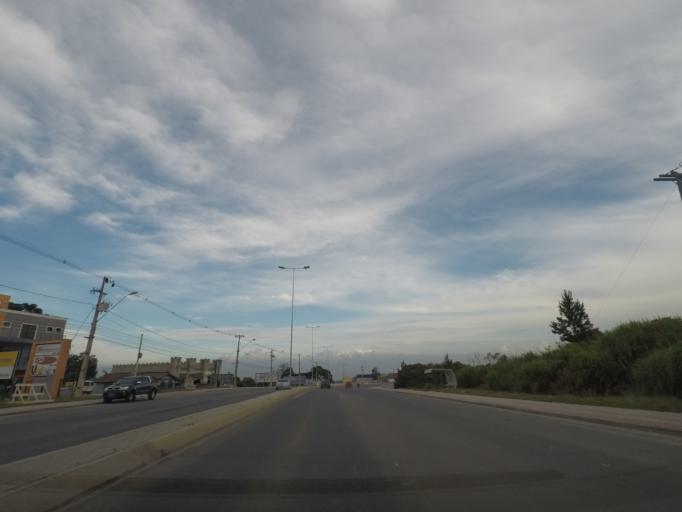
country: BR
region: Parana
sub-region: Colombo
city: Colombo
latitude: -25.2984
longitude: -49.2235
